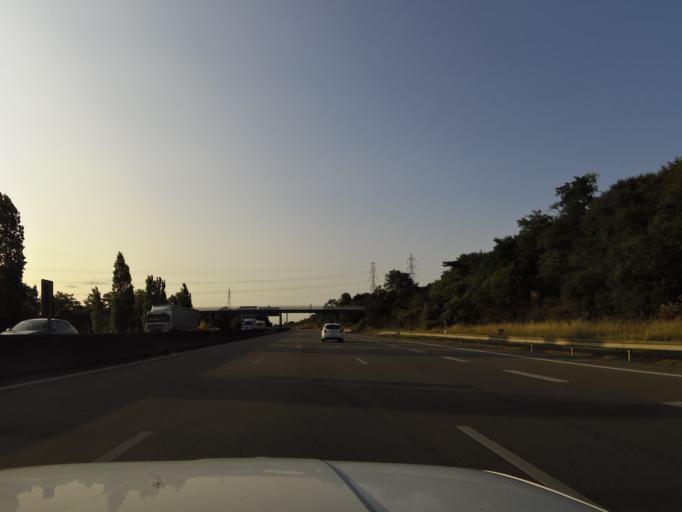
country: FR
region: Rhone-Alpes
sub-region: Departement de l'Isere
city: Chanas
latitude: 45.3248
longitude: 4.8121
